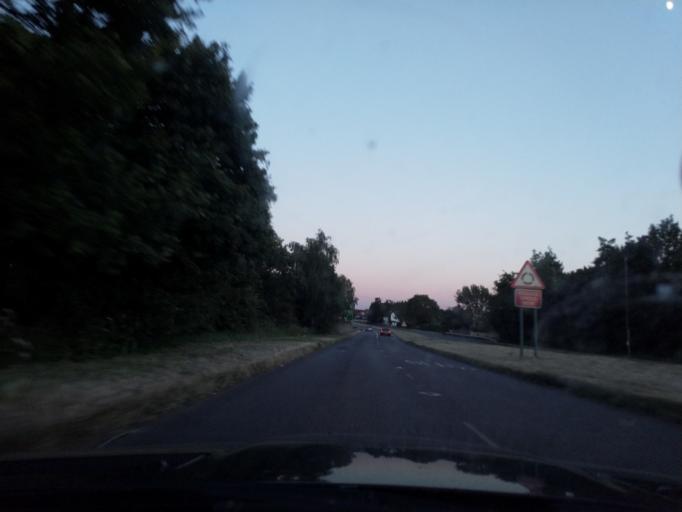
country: GB
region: England
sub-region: Solihull
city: Balsall Common
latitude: 52.4046
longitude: -1.6594
